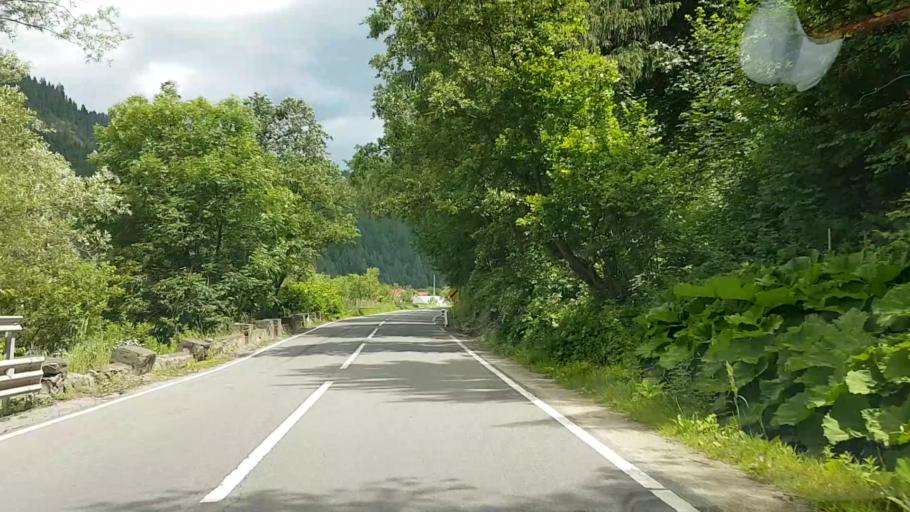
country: RO
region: Neamt
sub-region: Comuna Farcasa
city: Farcasa
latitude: 47.1356
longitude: 25.8837
